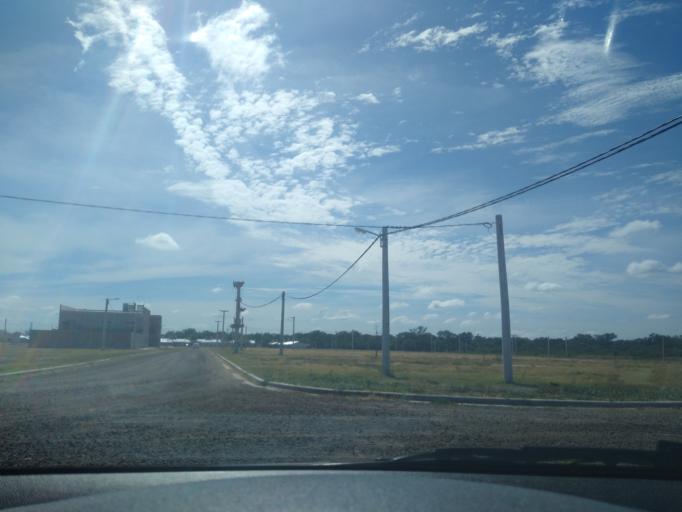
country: AR
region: Chaco
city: Resistencia
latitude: -27.4155
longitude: -58.9592
